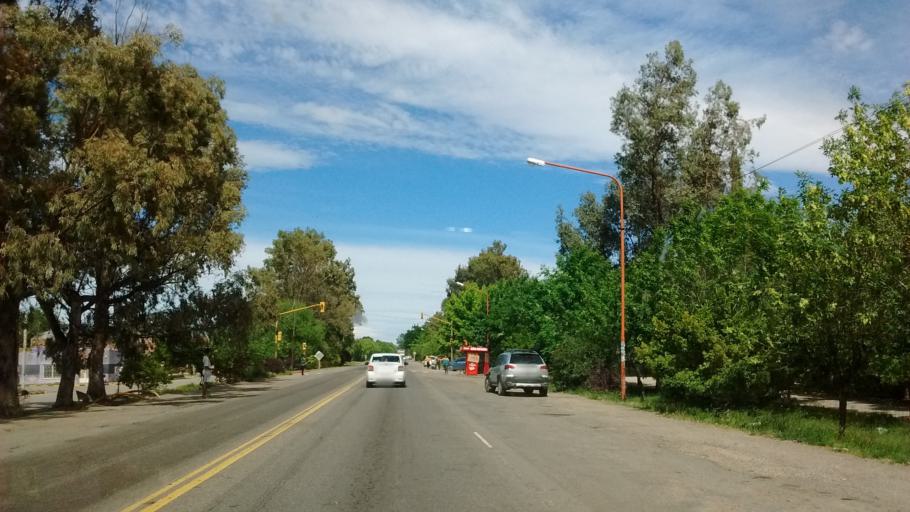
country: AR
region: Neuquen
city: Senillosa
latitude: -39.0096
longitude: -68.4268
